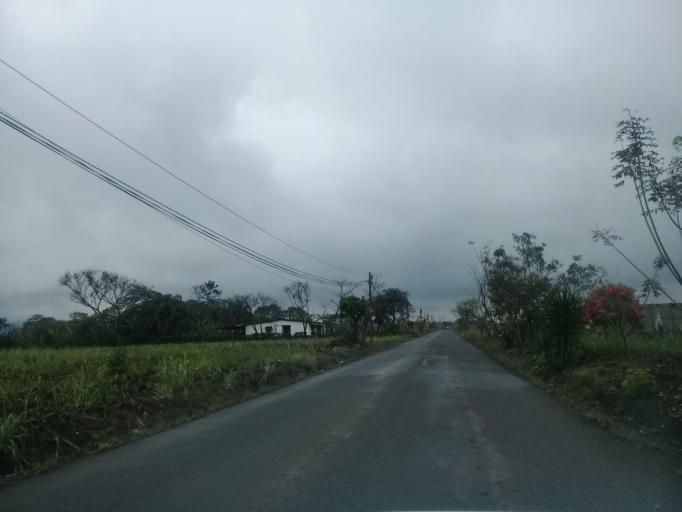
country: MX
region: Veracruz
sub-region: Cordoba
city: San Jose de Tapia
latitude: 18.8328
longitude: -96.9561
